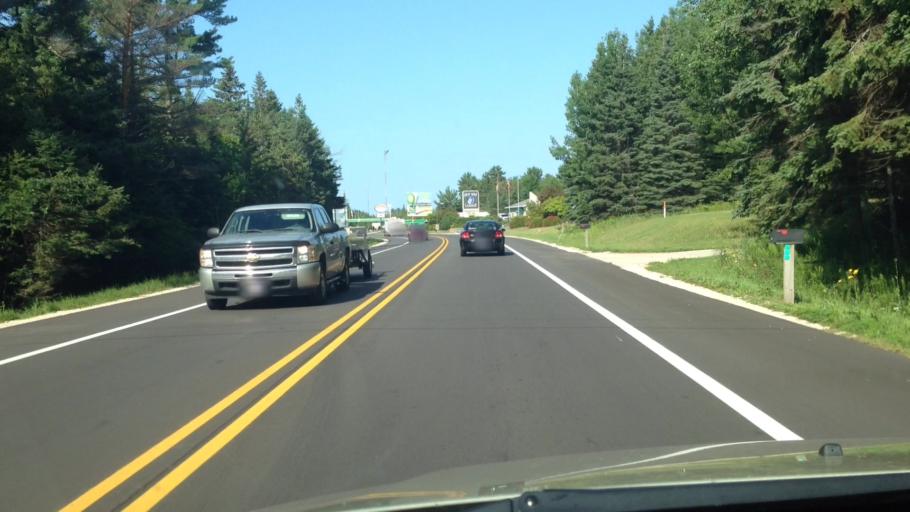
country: US
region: Michigan
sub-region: Schoolcraft County
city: Manistique
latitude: 45.9621
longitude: -86.2161
